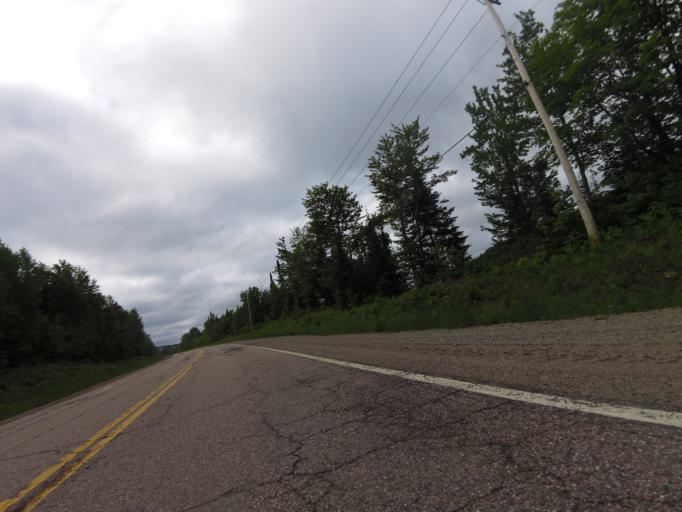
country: CA
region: Quebec
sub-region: Outaouais
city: Shawville
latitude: 45.8254
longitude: -76.4613
